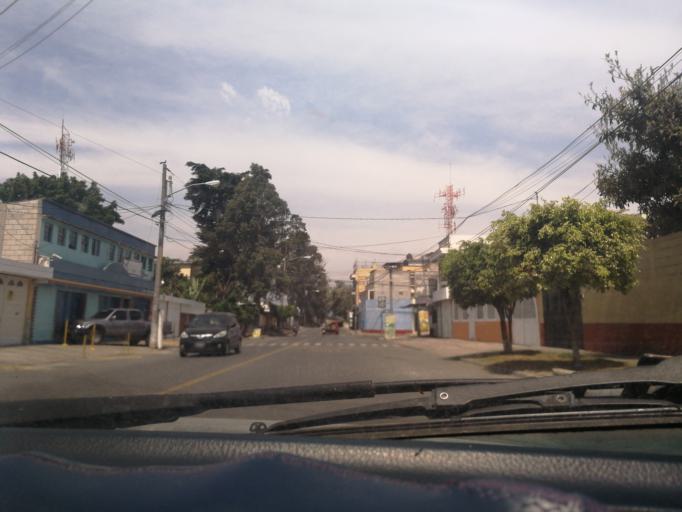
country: GT
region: Guatemala
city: Guatemala City
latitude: 14.6230
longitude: -90.4796
